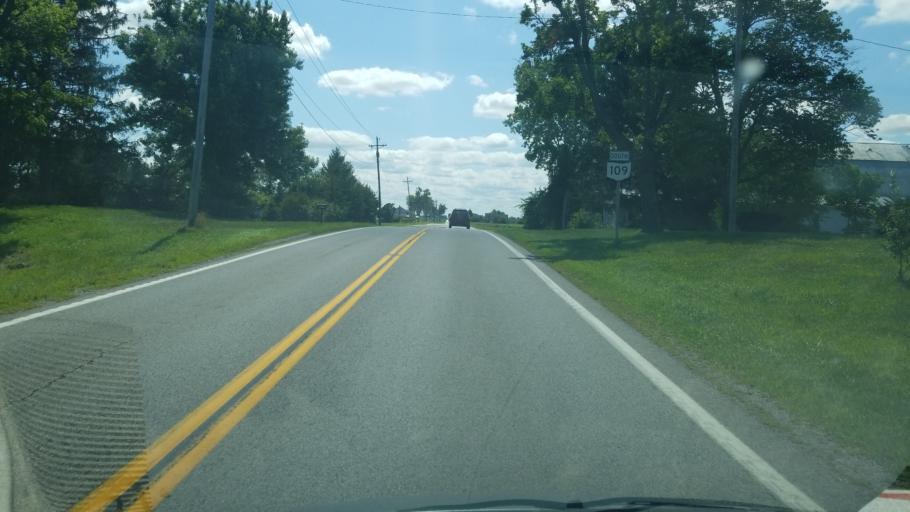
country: US
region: Ohio
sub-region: Fulton County
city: Delta
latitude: 41.6564
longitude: -84.0354
